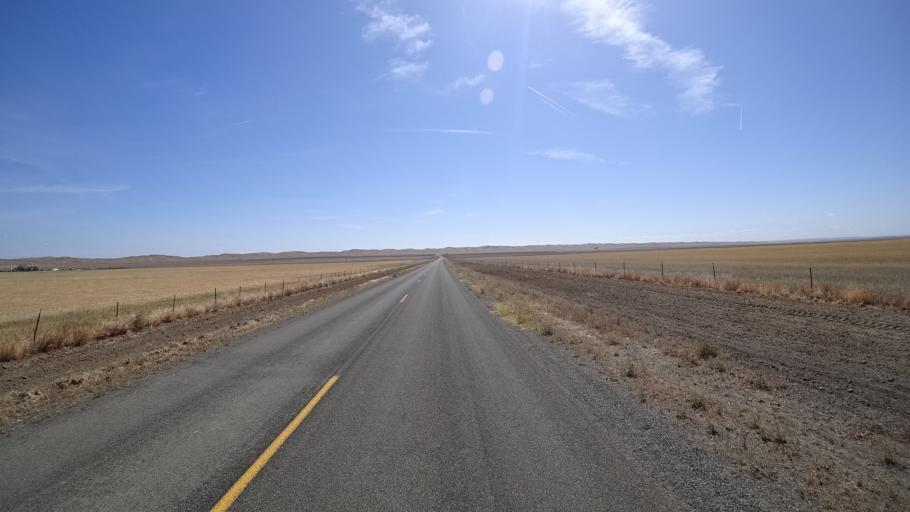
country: US
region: California
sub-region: Kings County
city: Avenal
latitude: 35.9351
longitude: -120.0633
